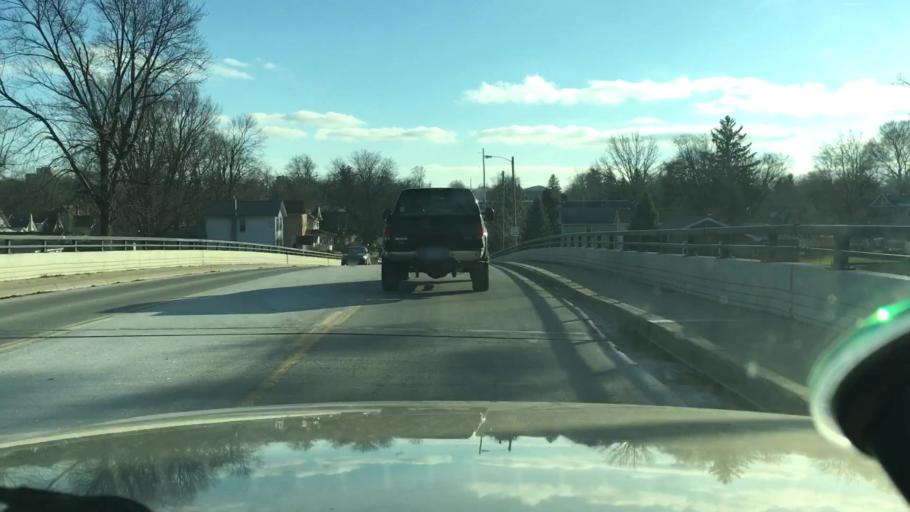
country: US
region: Michigan
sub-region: Jackson County
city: Jackson
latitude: 42.2534
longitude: -84.4235
